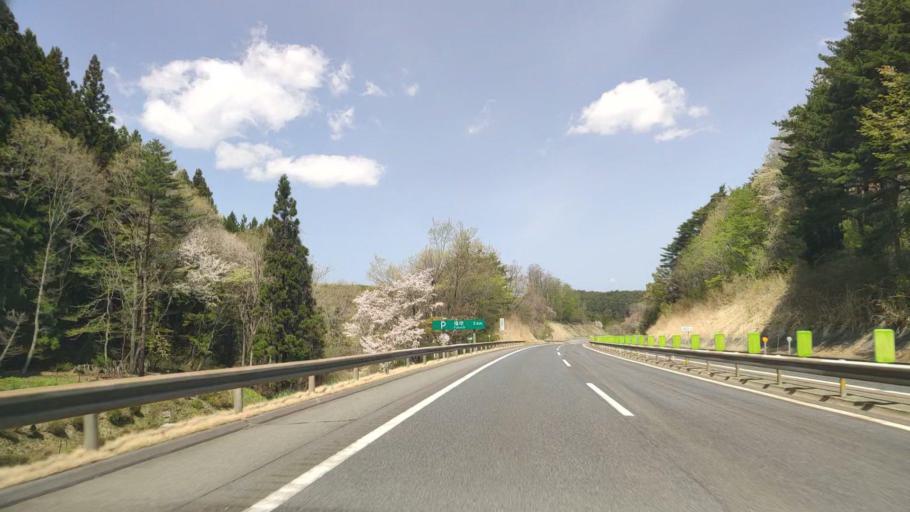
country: JP
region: Aomori
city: Hachinohe
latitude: 40.4182
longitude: 141.4403
